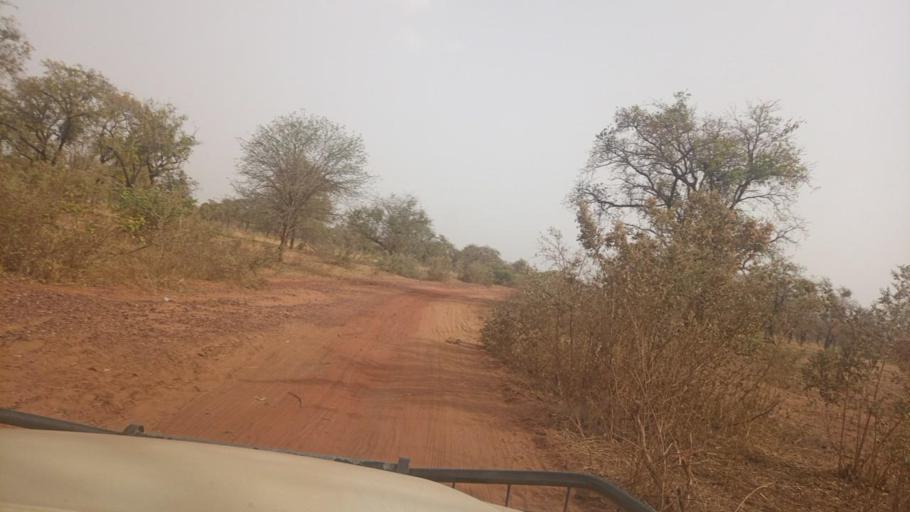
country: BF
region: Boucle du Mouhoun
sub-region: Province des Banwa
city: Salanso
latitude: 12.1074
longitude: -4.3355
